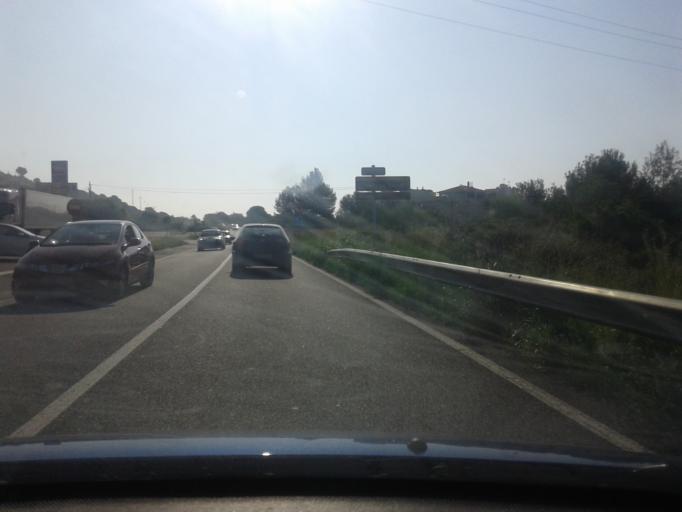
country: ES
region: Catalonia
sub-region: Provincia de Barcelona
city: Sitges
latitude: 41.2384
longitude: 1.8267
